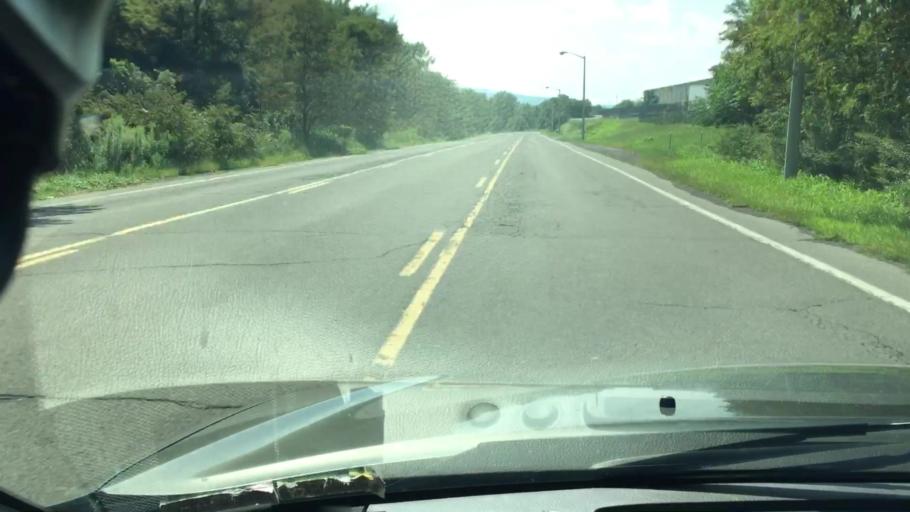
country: US
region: Pennsylvania
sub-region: Luzerne County
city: Plymouth
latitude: 41.2003
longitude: -75.9381
